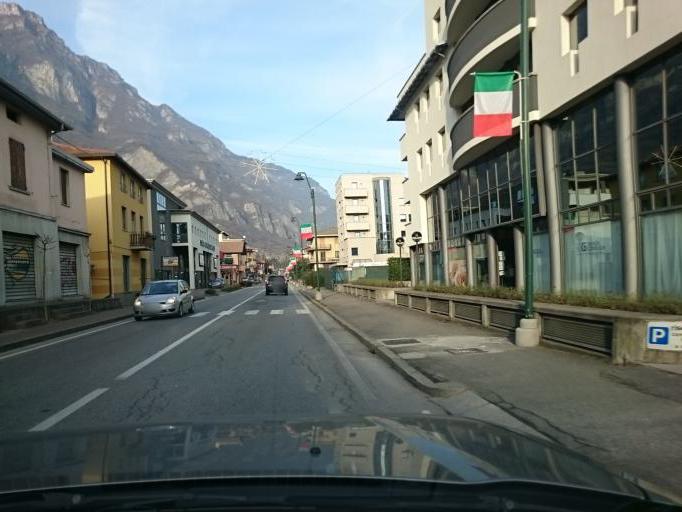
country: IT
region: Lombardy
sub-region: Provincia di Brescia
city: Darfo Boario Terme
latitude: 45.8939
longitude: 10.1892
